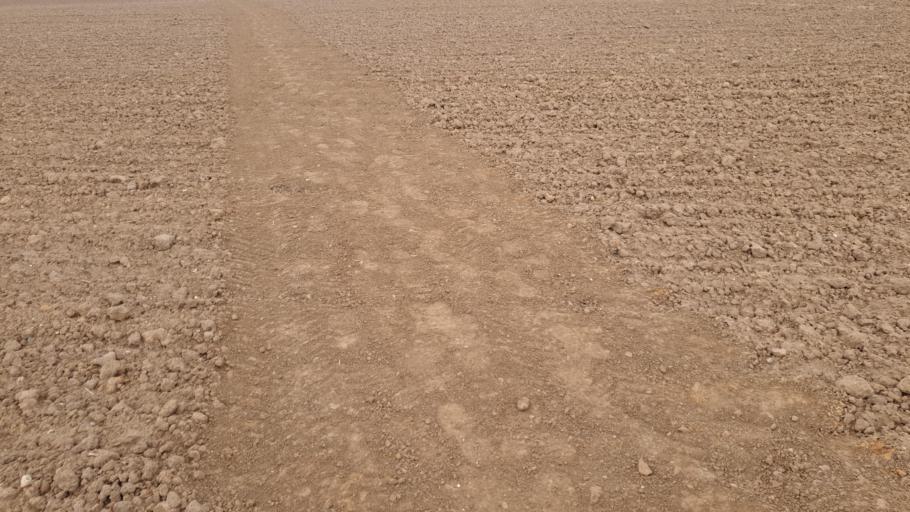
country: GB
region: England
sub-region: Essex
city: Great Bentley
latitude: 51.8459
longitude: 1.0724
